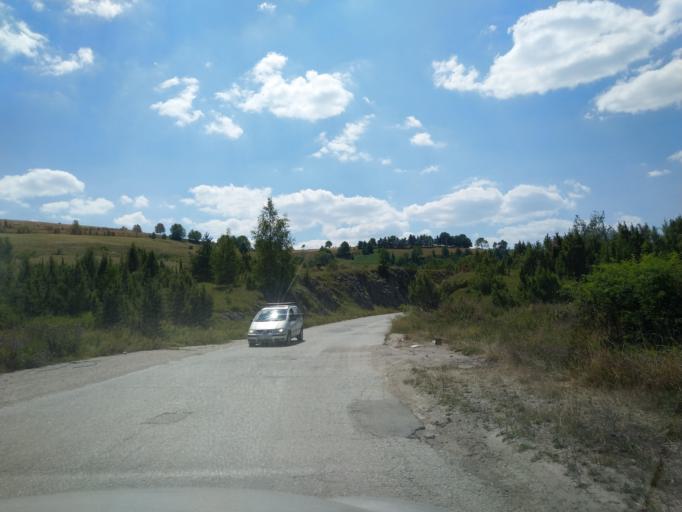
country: RS
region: Central Serbia
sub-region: Zlatiborski Okrug
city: Nova Varos
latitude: 43.4361
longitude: 19.9592
